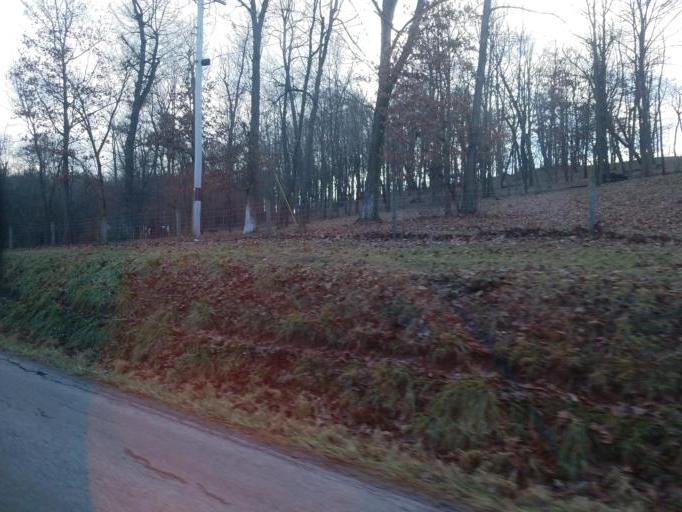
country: US
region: Ohio
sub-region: Sandusky County
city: Bellville
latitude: 40.5991
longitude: -82.3760
